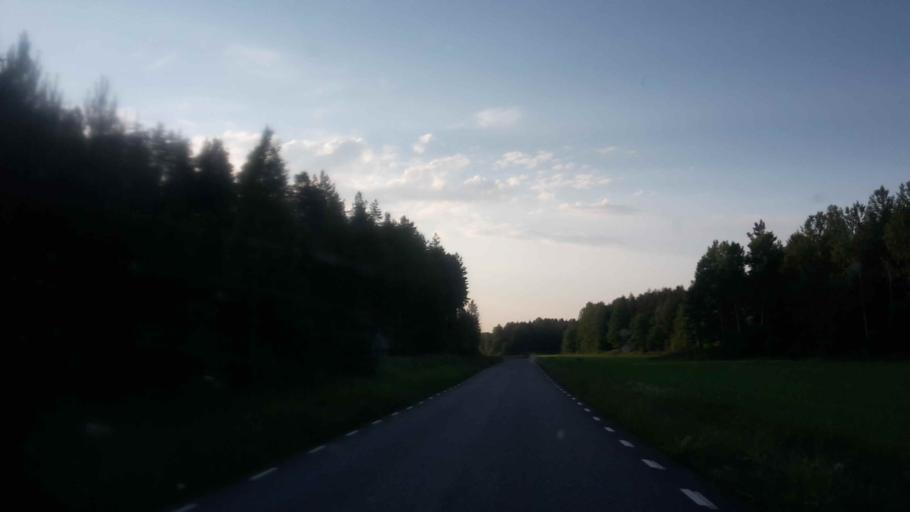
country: SE
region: OEstergoetland
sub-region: Valdemarsviks Kommun
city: Valdemarsvik
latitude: 58.2987
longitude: 16.6612
